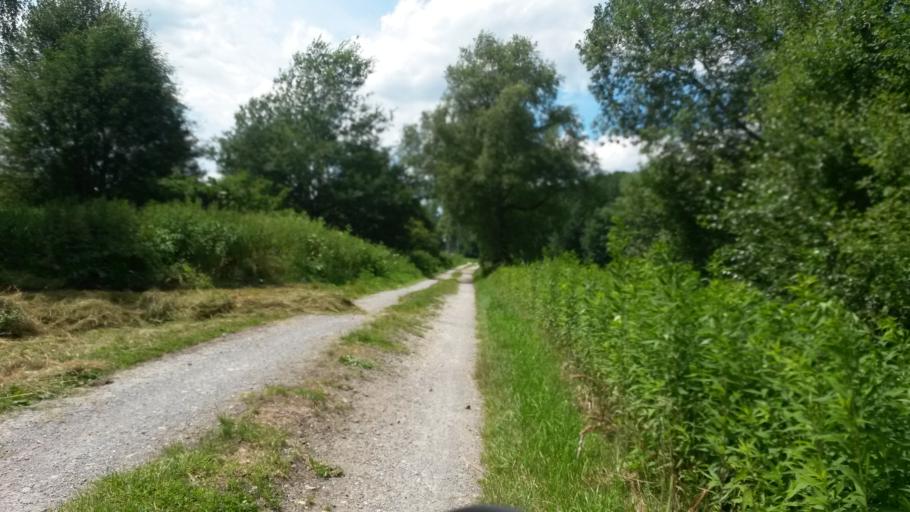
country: DE
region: Bavaria
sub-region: Upper Bavaria
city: Grassau
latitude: 47.8106
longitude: 12.4452
